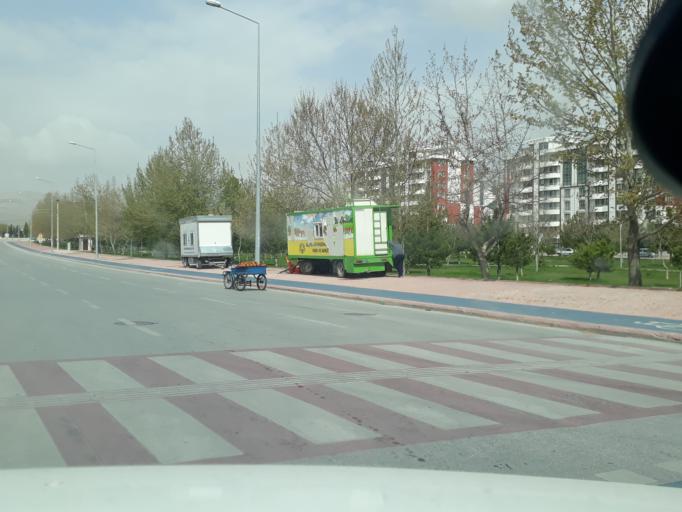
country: TR
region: Konya
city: Selcuklu
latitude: 37.9425
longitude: 32.4930
